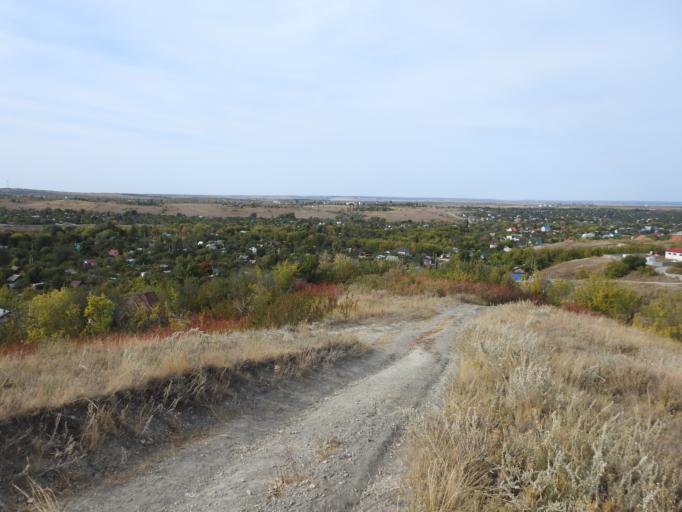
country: RU
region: Saratov
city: Sokolovyy
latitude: 51.5704
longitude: 45.8755
